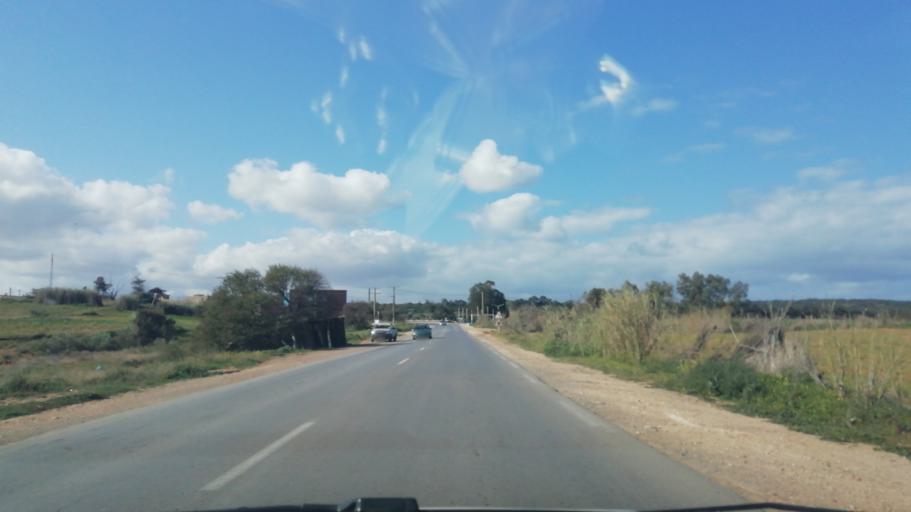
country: DZ
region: Relizane
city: Mazouna
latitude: 36.3005
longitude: 0.6609
